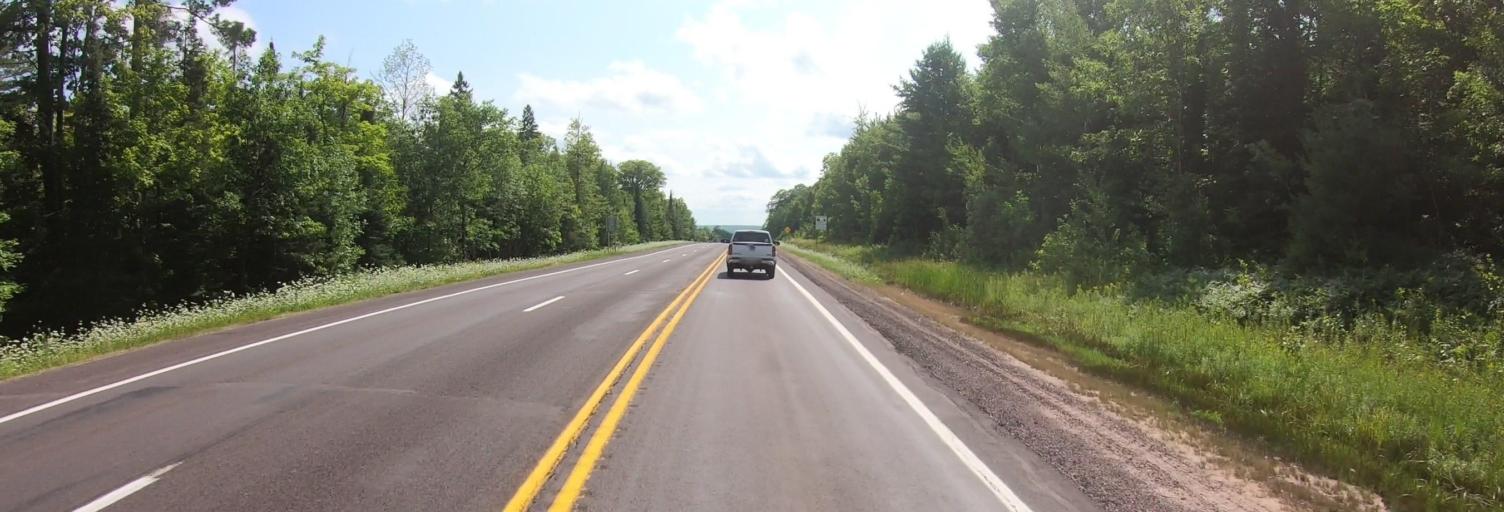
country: US
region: Michigan
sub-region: Ontonagon County
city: Ontonagon
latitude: 46.8079
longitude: -88.9972
